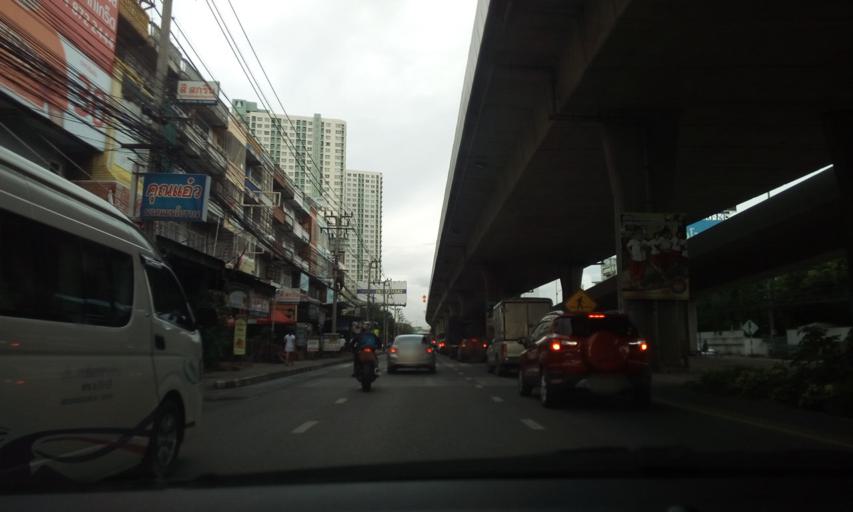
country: TH
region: Nonthaburi
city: Pak Kret
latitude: 13.9102
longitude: 100.4995
